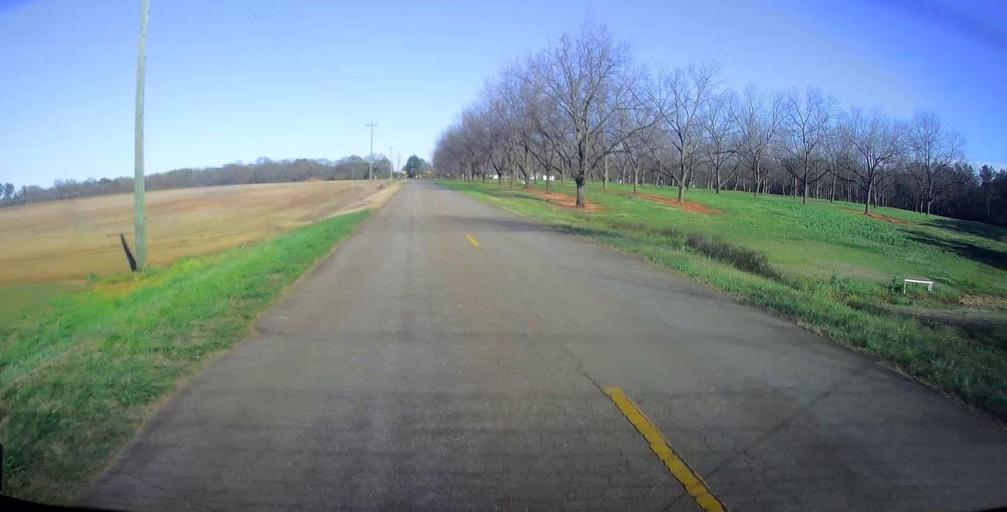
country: US
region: Georgia
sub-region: Macon County
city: Marshallville
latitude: 32.5116
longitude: -83.9288
